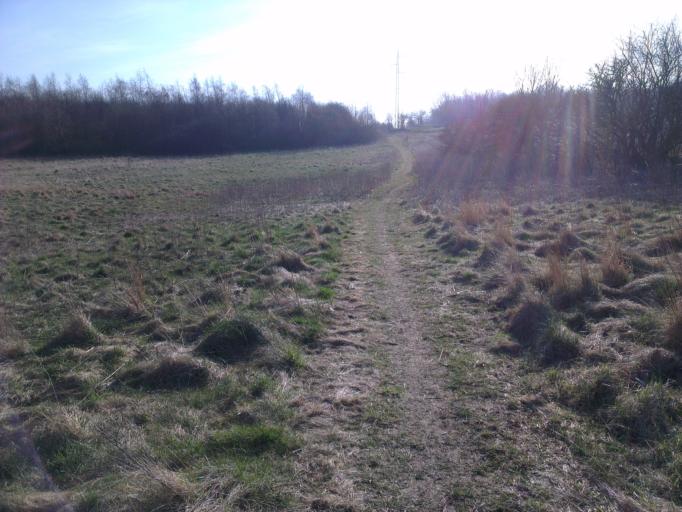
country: DK
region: Capital Region
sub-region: Frederikssund Kommune
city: Frederikssund
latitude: 55.8421
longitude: 12.0816
